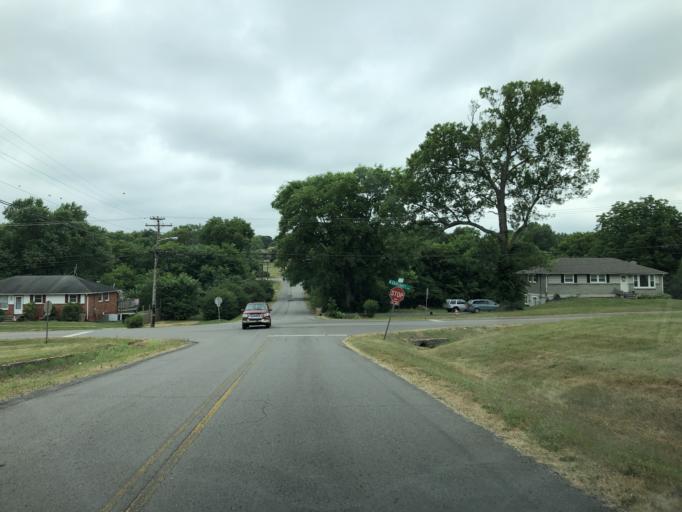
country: US
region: Tennessee
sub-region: Davidson County
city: Goodlettsville
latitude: 36.2791
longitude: -86.7241
